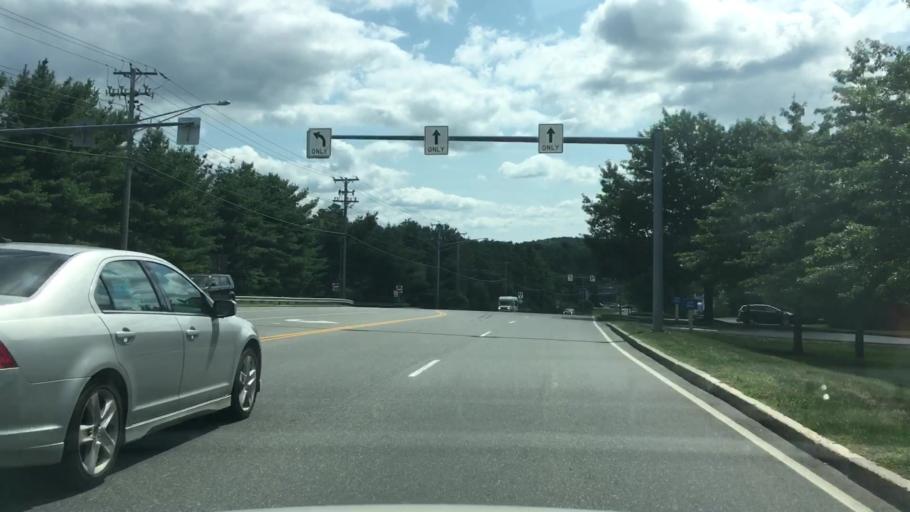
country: US
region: Maine
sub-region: Kennebec County
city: Augusta
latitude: 44.3429
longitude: -69.7931
